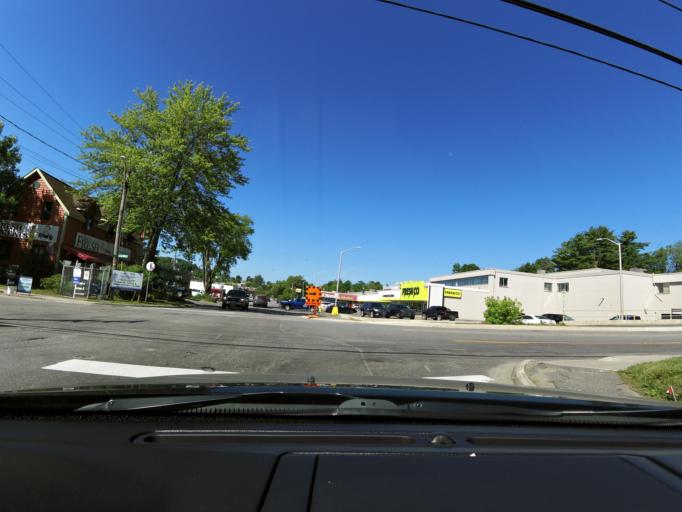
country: CA
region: Ontario
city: Huntsville
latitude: 45.3299
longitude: -79.2129
